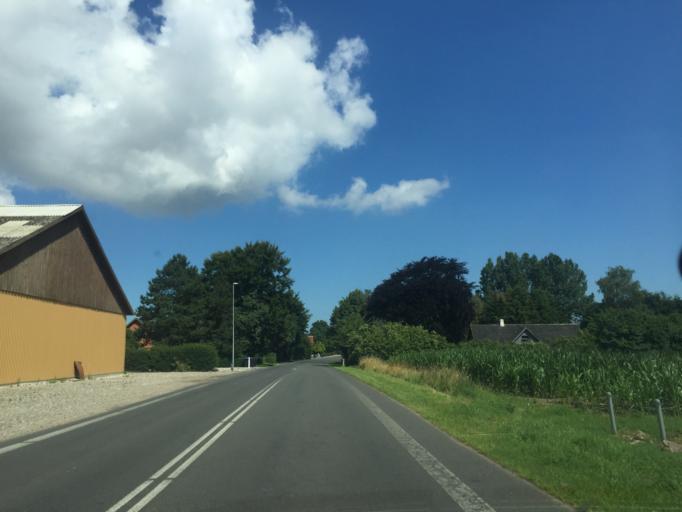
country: DK
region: South Denmark
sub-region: Nordfyns Kommune
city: Otterup
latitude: 55.5361
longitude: 10.3859
